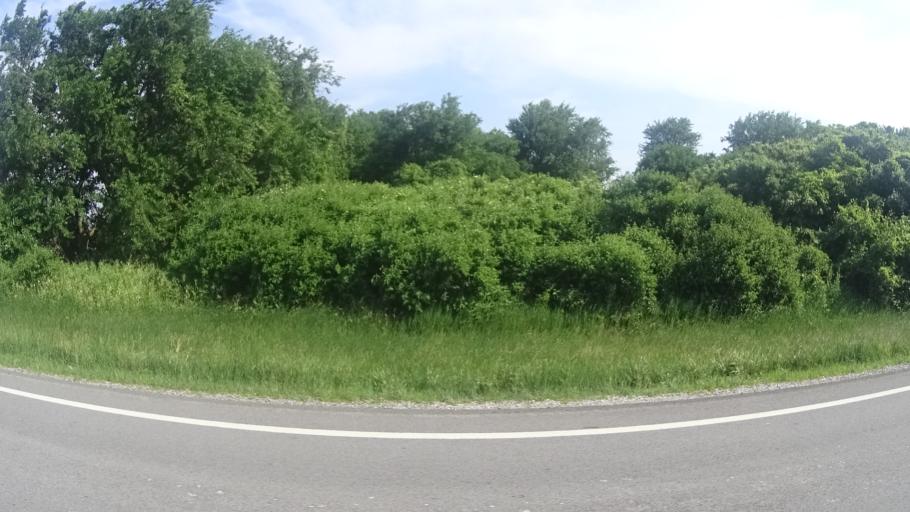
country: US
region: Ohio
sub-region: Huron County
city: Bellevue
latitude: 41.2920
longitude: -82.7637
